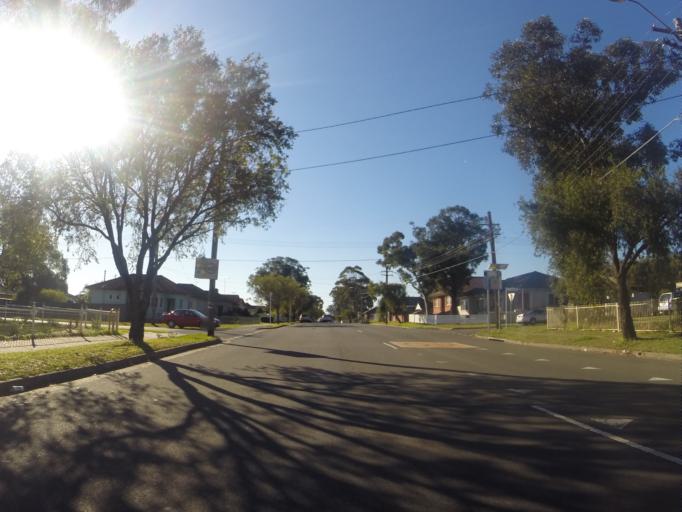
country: AU
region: New South Wales
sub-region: Bankstown
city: Regents Park
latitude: -33.8950
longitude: 151.0213
